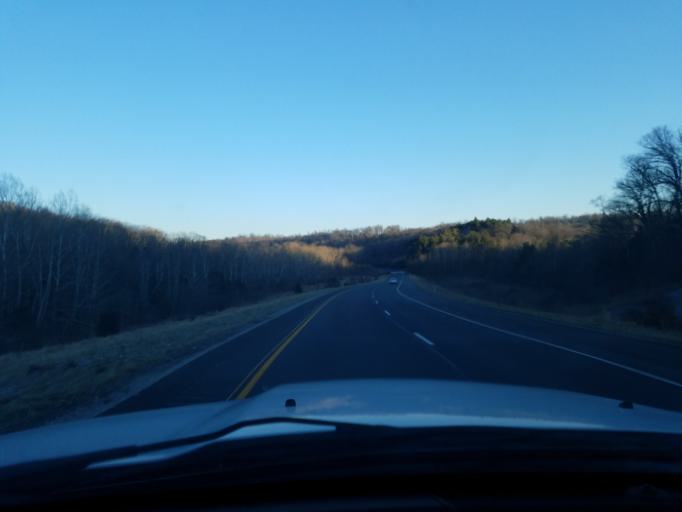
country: US
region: Indiana
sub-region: Crawford County
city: English
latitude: 38.2420
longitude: -86.4105
